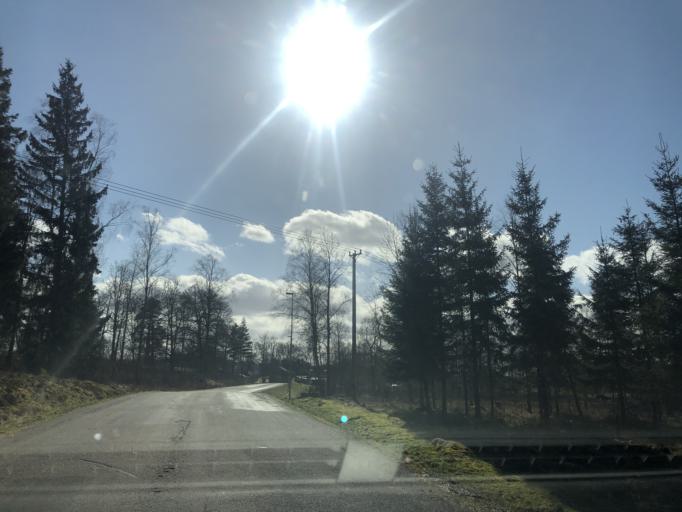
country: SE
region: Vaestra Goetaland
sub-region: Ulricehamns Kommun
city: Ulricehamn
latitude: 57.6897
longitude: 13.4183
